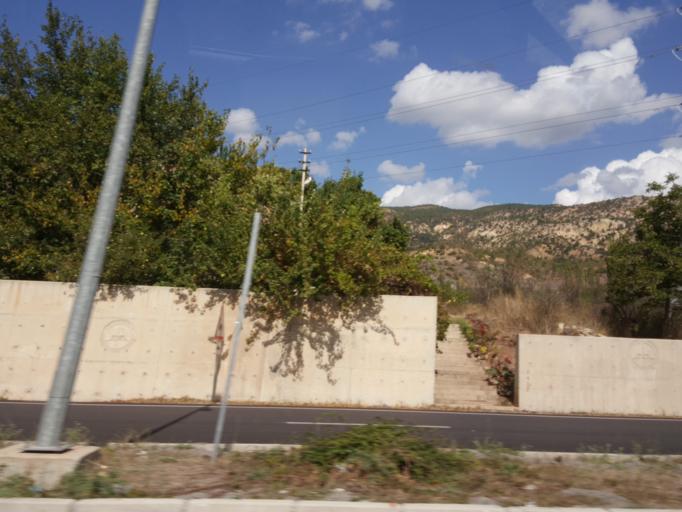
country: TR
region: Sivas
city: Koyulhisar
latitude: 40.2883
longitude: 37.7910
